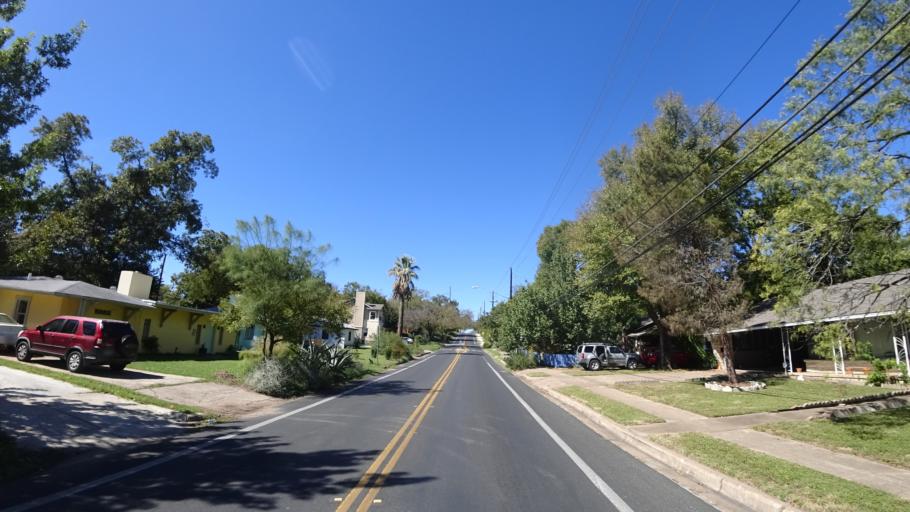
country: US
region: Texas
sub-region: Travis County
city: Austin
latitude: 30.2910
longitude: -97.7119
